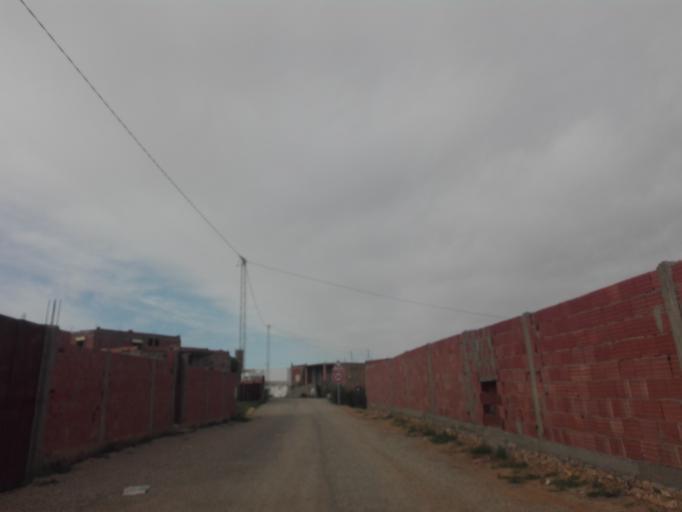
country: TN
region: Safaqis
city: Sfax
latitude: 34.7302
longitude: 10.4929
